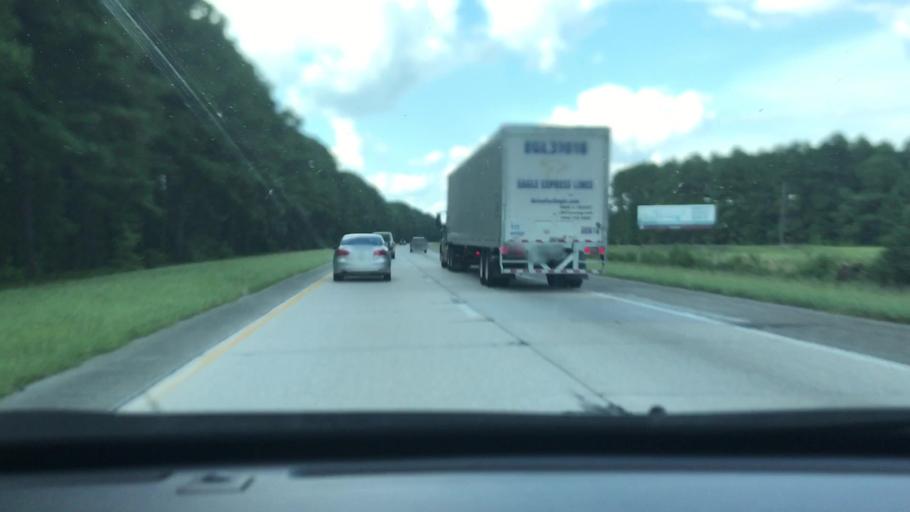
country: US
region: South Carolina
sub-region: Florence County
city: Timmonsville
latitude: 34.0570
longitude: -79.9696
